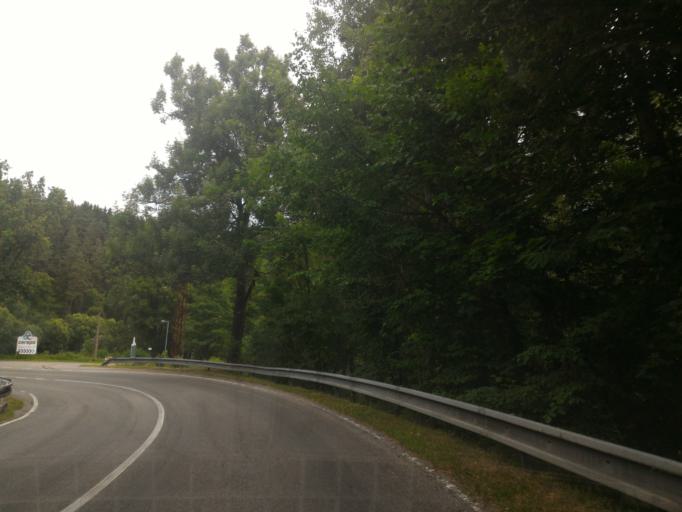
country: CZ
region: Vysocina
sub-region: Okres Pelhrimov
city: Zeliv
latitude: 49.5289
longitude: 15.1721
